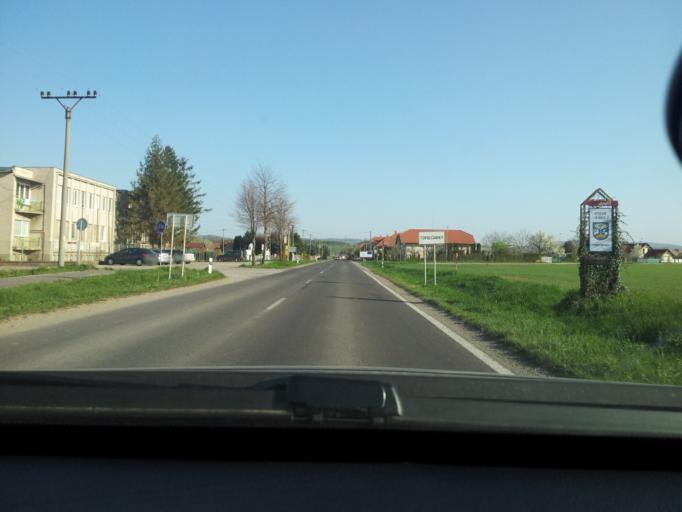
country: SK
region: Nitriansky
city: Zlate Moravce
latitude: 48.4075
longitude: 18.4106
